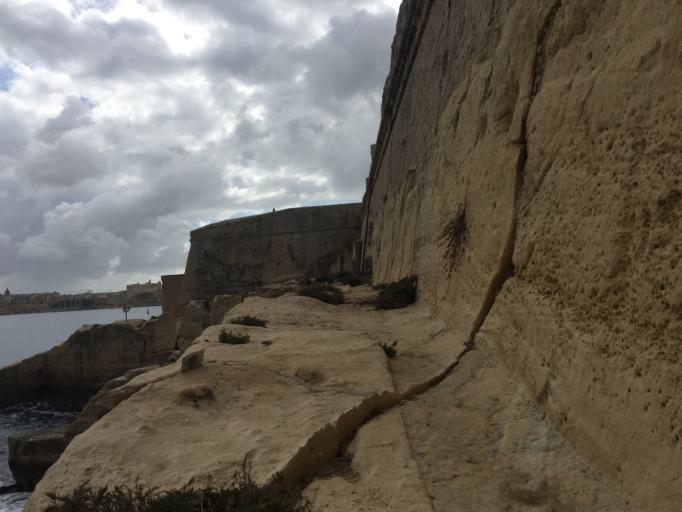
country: MT
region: Il-Belt Valletta
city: Valletta
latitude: 35.9014
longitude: 14.5193
